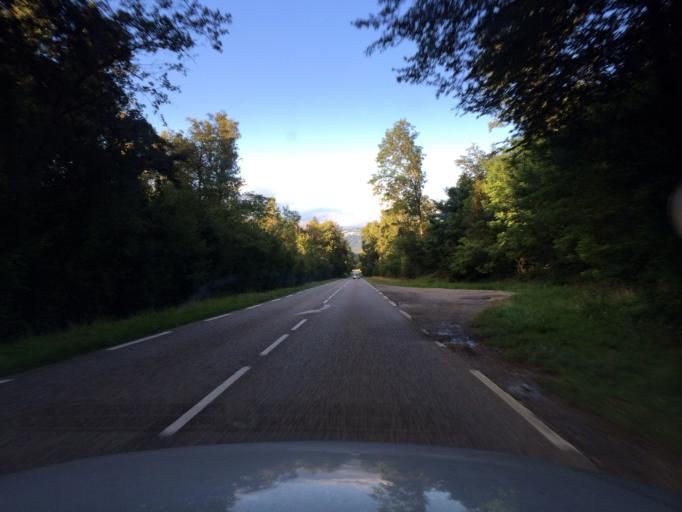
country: FR
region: Rhone-Alpes
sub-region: Departement de la Haute-Savoie
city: Frangy
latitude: 45.9968
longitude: 5.8531
